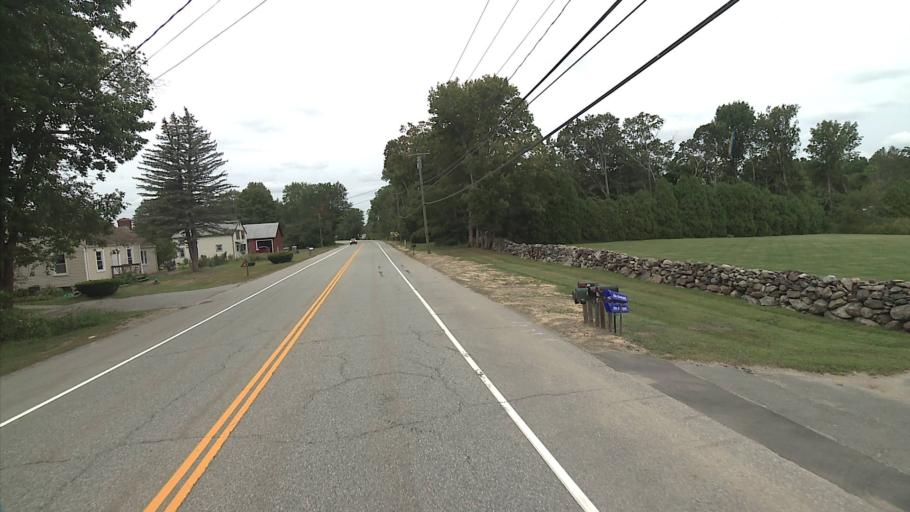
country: US
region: Connecticut
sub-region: Tolland County
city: Hebron
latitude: 41.6700
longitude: -72.3802
